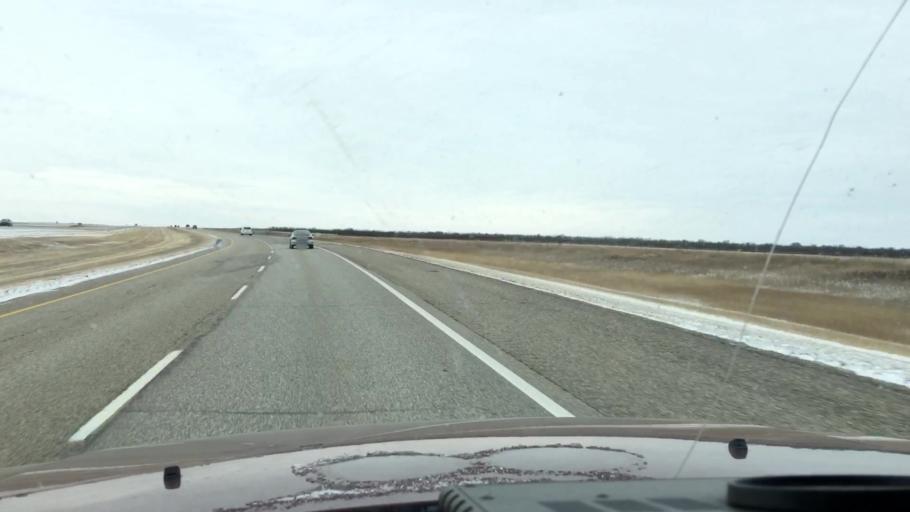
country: CA
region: Saskatchewan
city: Saskatoon
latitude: 51.4710
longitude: -106.2474
